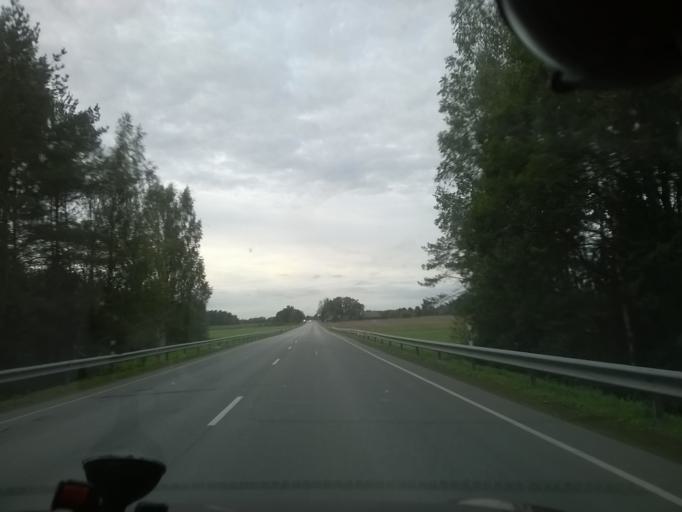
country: EE
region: Vorumaa
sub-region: Voru linn
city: Voru
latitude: 57.9001
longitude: 26.8388
